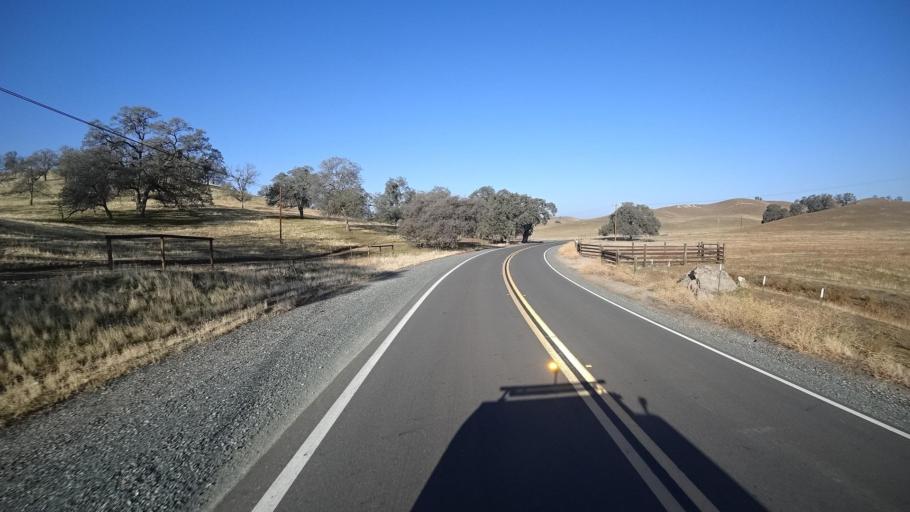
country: US
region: California
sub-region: Tulare County
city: Richgrove
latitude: 35.7140
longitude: -118.8606
